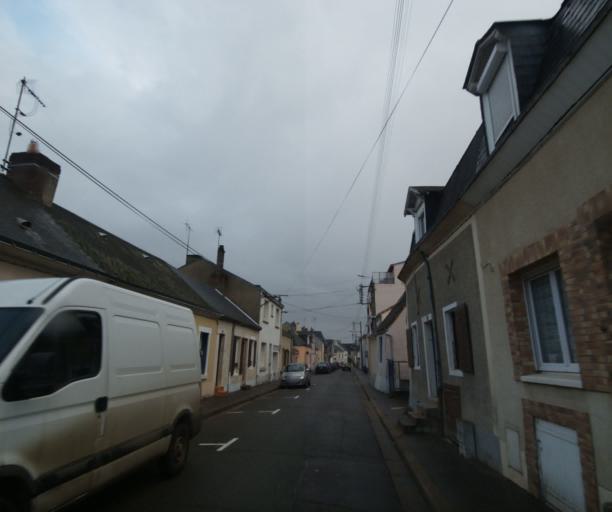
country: FR
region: Pays de la Loire
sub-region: Departement de la Sarthe
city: Coulaines
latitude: 48.0155
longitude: 0.1891
